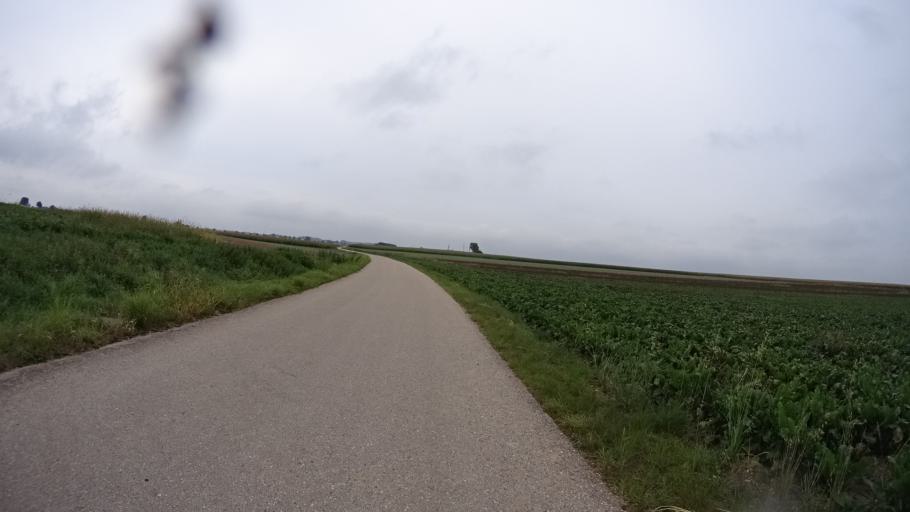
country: DE
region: Bavaria
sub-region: Upper Bavaria
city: Gaimersheim
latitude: 48.8247
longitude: 11.3620
